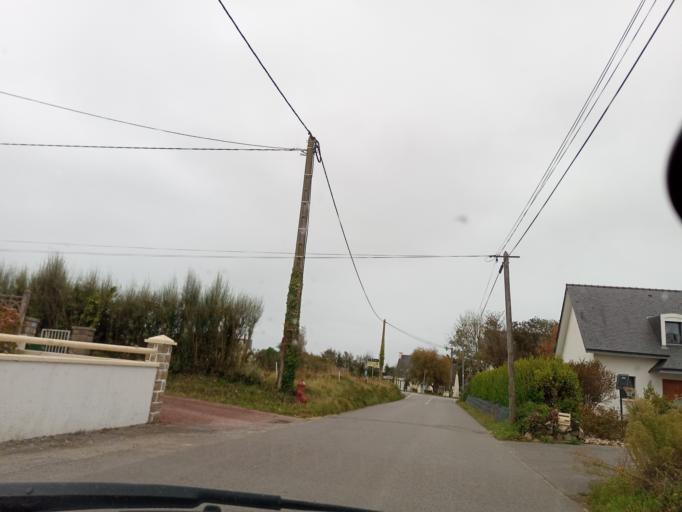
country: FR
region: Brittany
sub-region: Departement du Finistere
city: Esquibien
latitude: 48.0205
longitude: -4.5638
